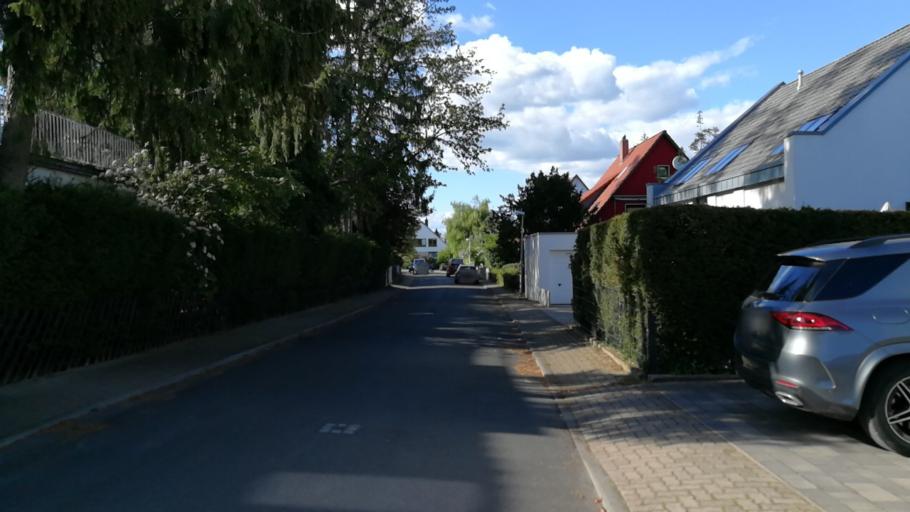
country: DE
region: Lower Saxony
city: Gehrden
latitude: 52.3107
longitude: 9.5945
